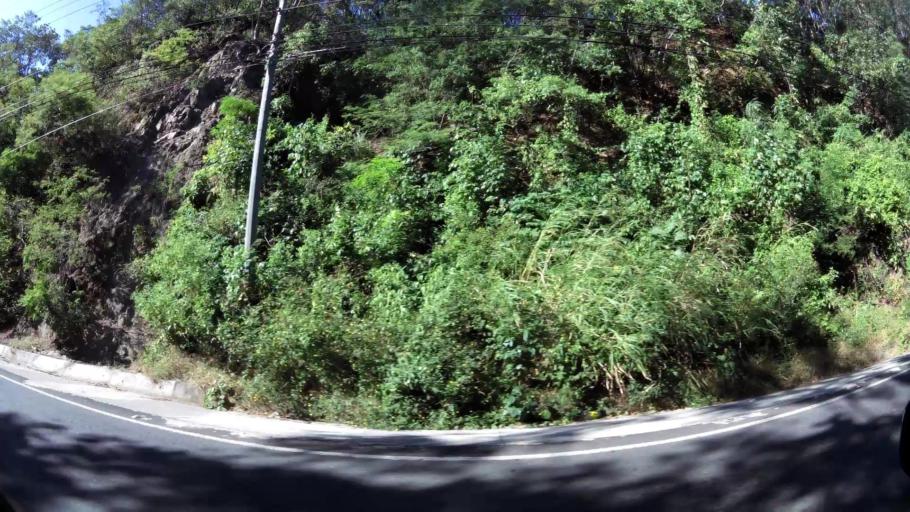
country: CR
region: Guanacaste
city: Belen
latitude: 10.3660
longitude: -85.7573
